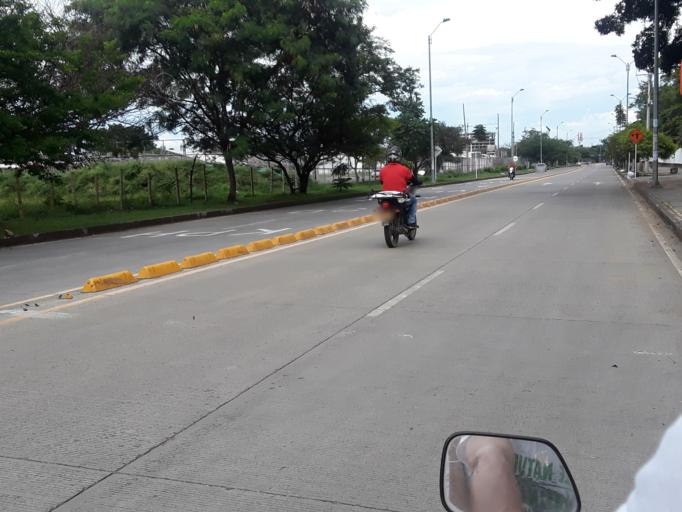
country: CO
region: Valle del Cauca
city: Cali
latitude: 3.4174
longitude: -76.5531
